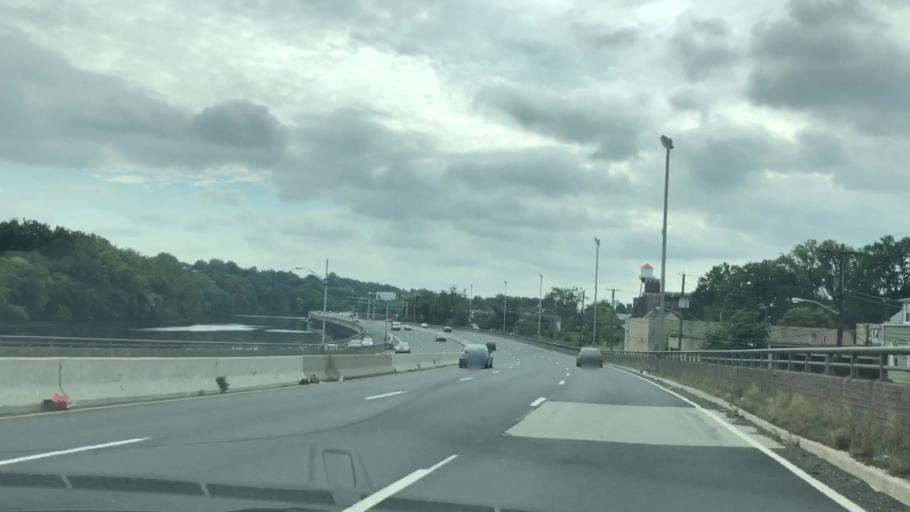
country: US
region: New Jersey
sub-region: Essex County
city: Belleville
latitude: 40.7856
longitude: -74.1490
